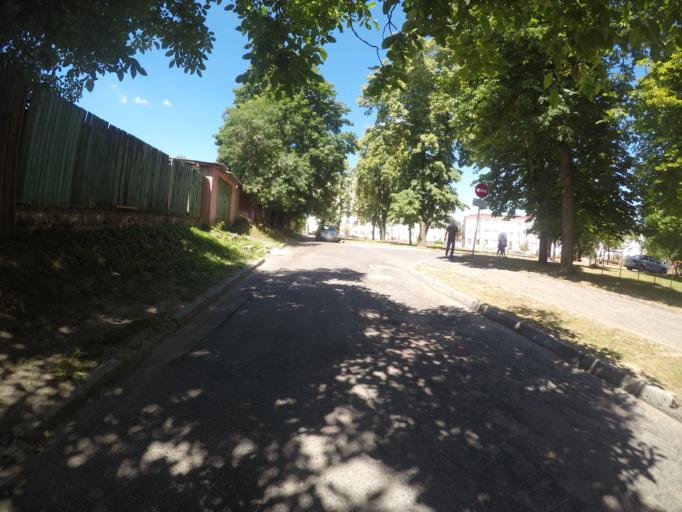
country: BY
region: Grodnenskaya
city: Hrodna
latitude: 53.6901
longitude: 23.8330
